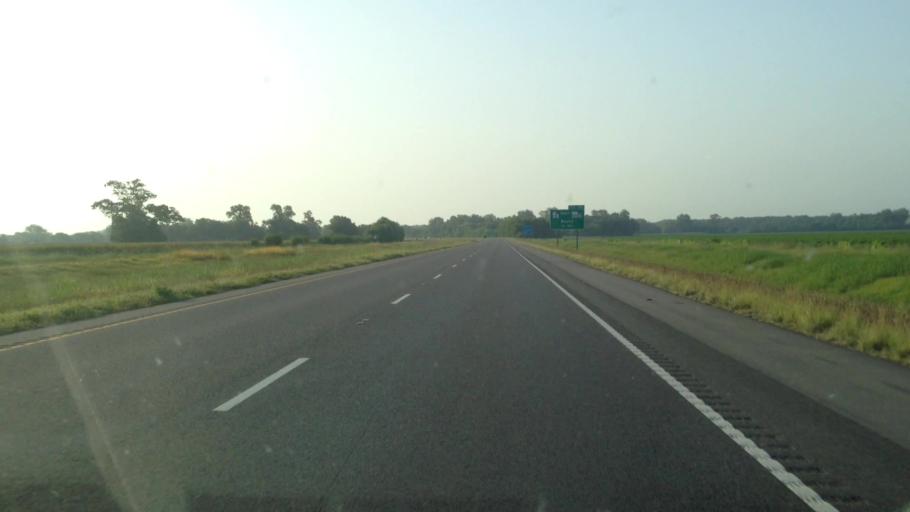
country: US
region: Louisiana
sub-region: Rapides Parish
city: Boyce
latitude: 31.3858
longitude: -92.6836
